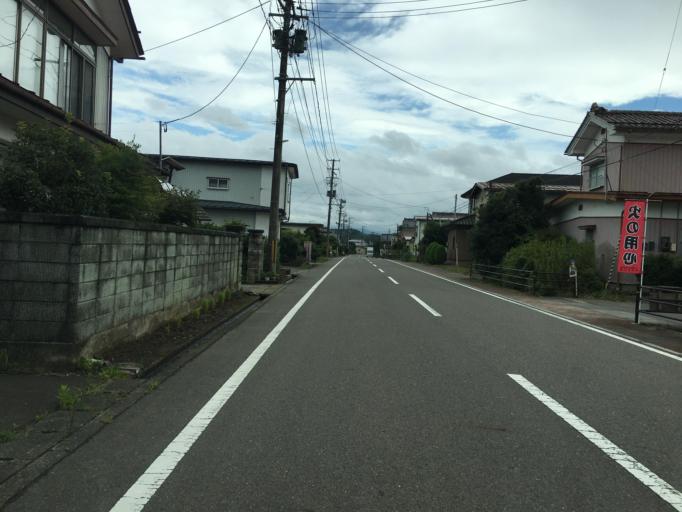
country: JP
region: Fukushima
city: Nihommatsu
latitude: 37.6250
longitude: 140.4582
